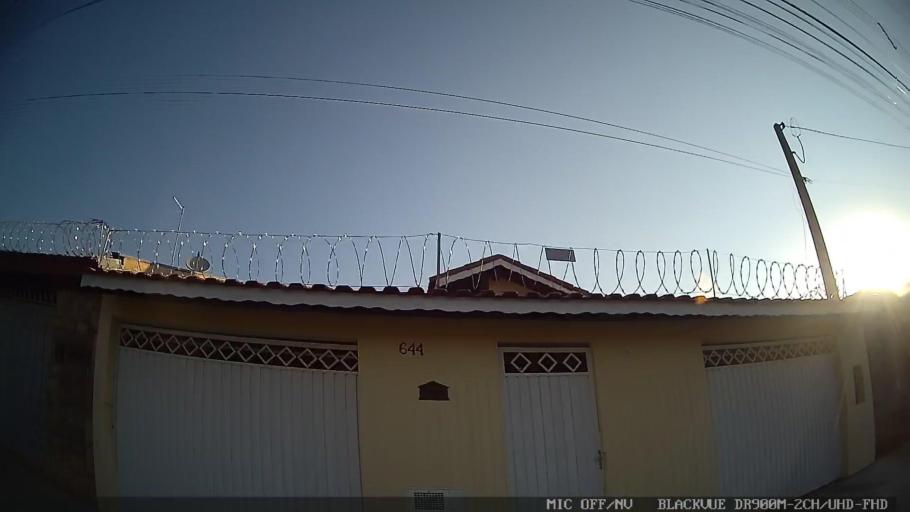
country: BR
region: Sao Paulo
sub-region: Cabreuva
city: Cabreuva
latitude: -23.2582
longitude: -47.0498
